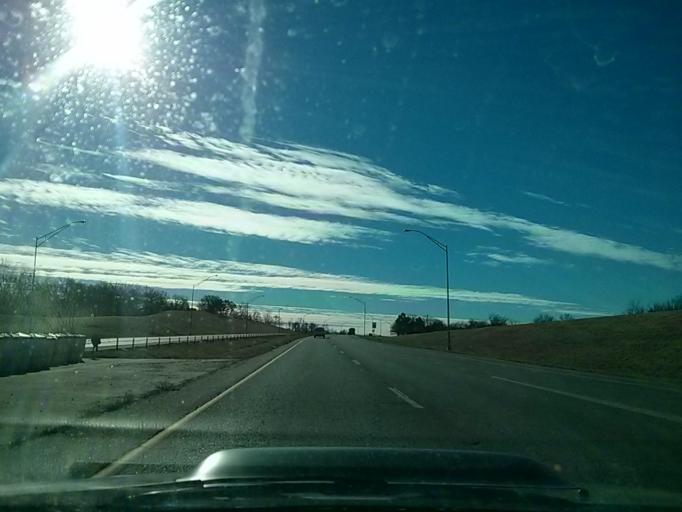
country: US
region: Oklahoma
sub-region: Tulsa County
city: Tulsa
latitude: 36.1015
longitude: -96.0081
